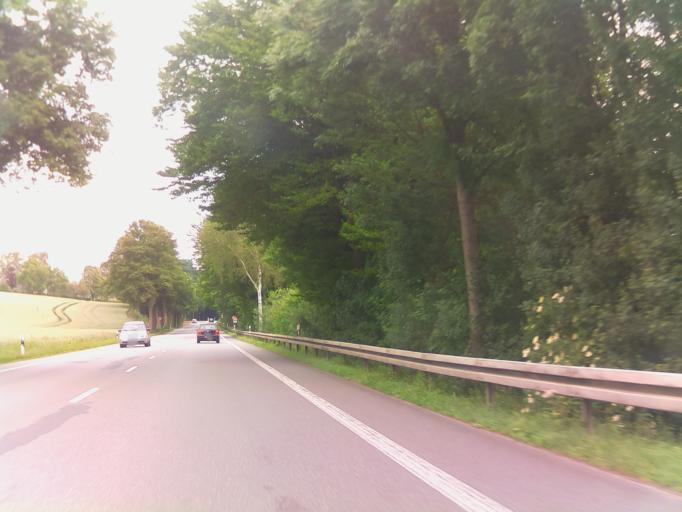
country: DE
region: North Rhine-Westphalia
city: Brakel
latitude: 51.6539
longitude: 9.1440
